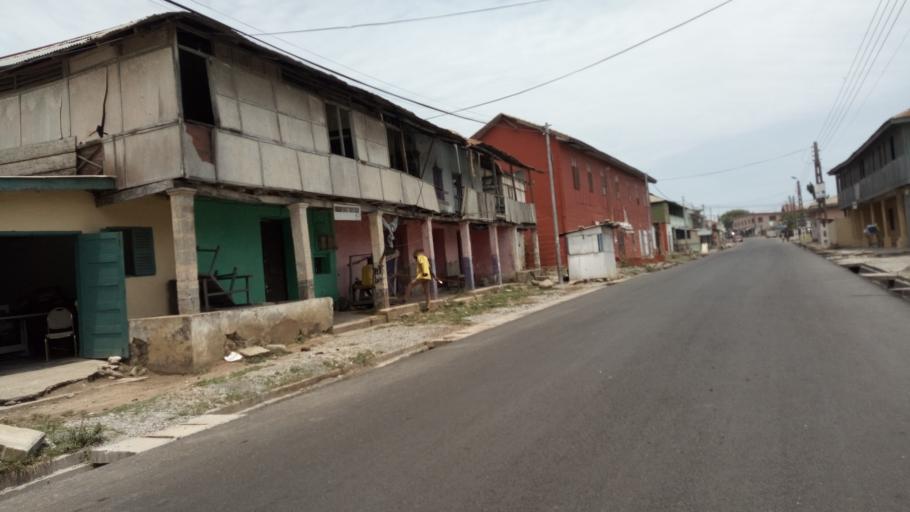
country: GH
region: Central
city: Winneba
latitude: 5.3426
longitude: -0.6262
